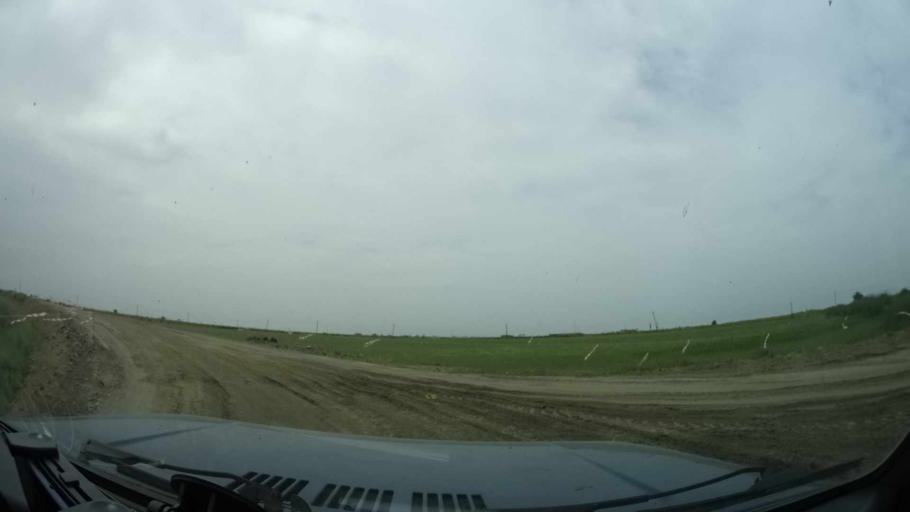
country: IR
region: Ardabil
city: Bileh Savar
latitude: 39.6167
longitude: 48.2178
